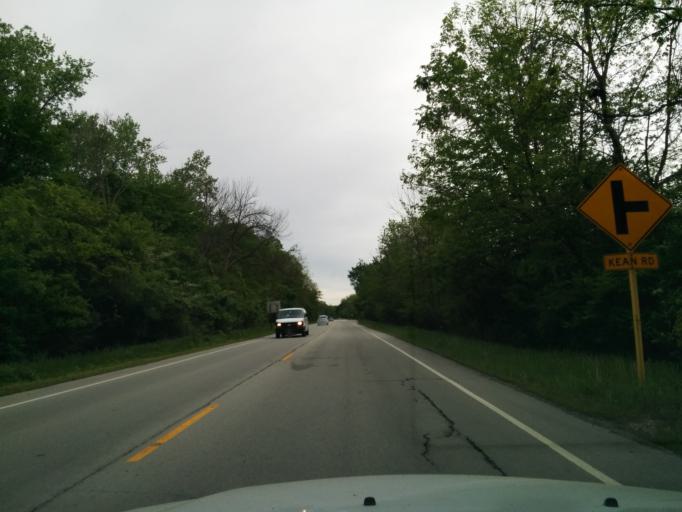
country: US
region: Illinois
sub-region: Cook County
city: Palos Park
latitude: 41.6830
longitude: -87.8484
